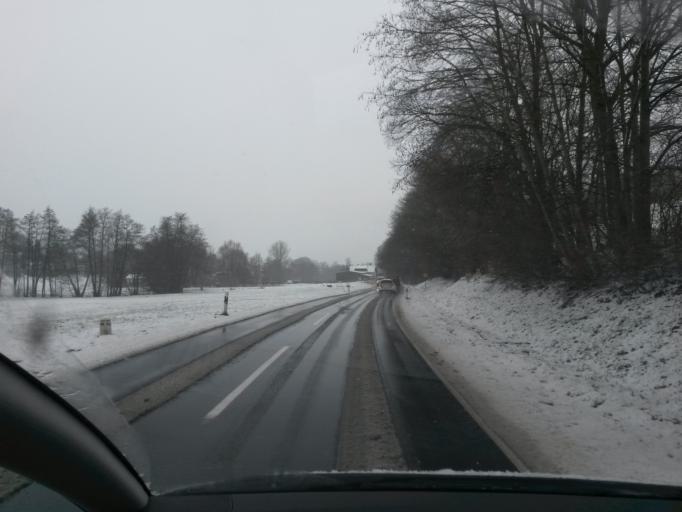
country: DE
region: Hesse
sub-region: Regierungsbezirk Kassel
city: Poppenhausen
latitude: 50.4835
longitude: 9.8136
